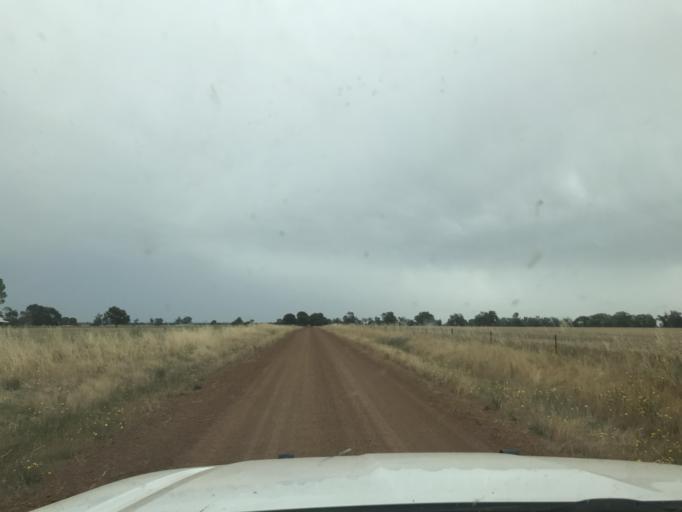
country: AU
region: Victoria
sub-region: Horsham
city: Horsham
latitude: -37.0630
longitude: 141.6381
